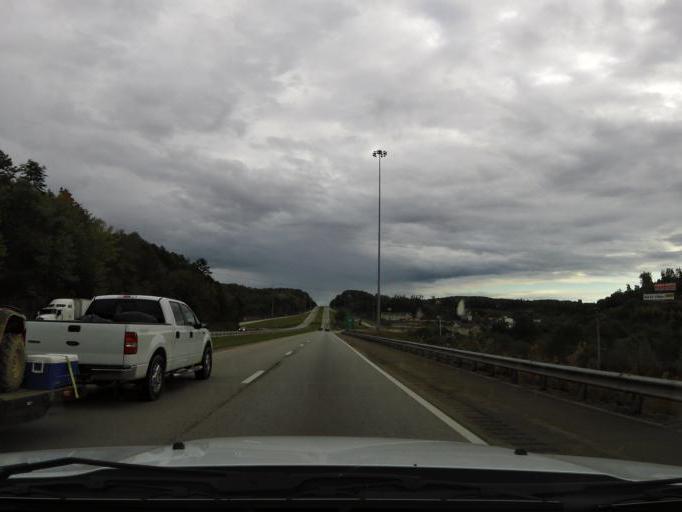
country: US
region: Kentucky
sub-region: Whitley County
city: Corbin
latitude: 36.9120
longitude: -84.1309
